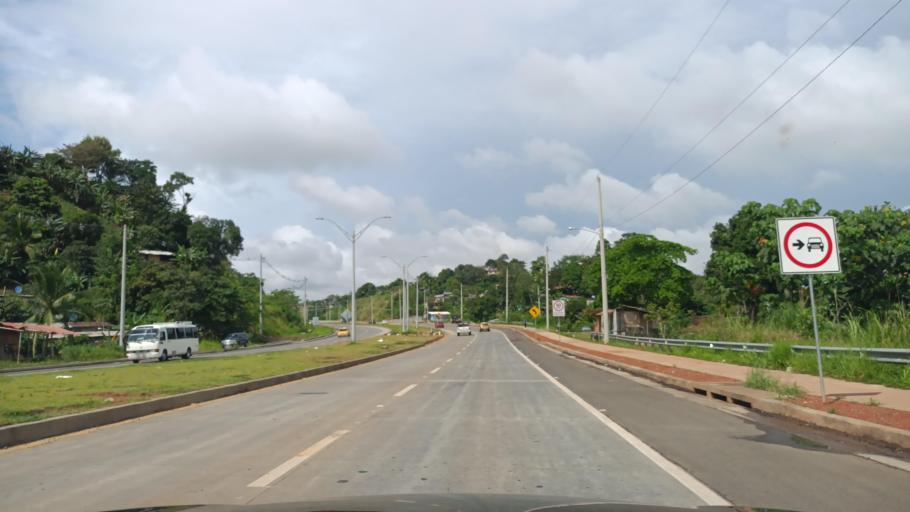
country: PA
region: Panama
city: Las Cumbres
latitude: 9.1015
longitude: -79.4928
